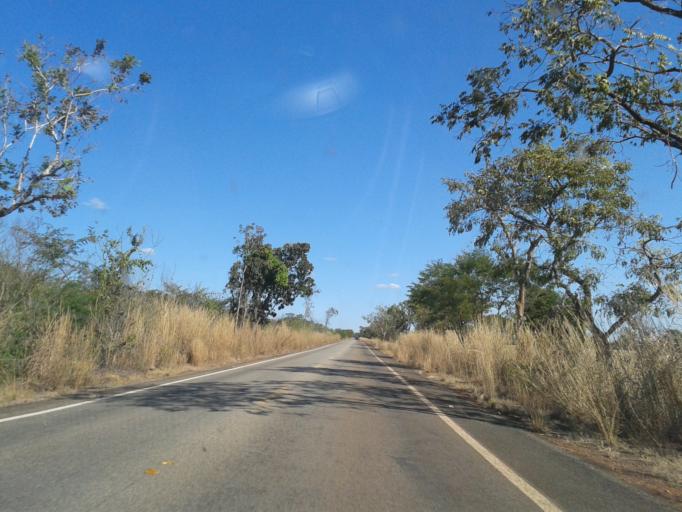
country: BR
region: Goias
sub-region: Mozarlandia
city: Mozarlandia
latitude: -14.2921
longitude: -50.4025
